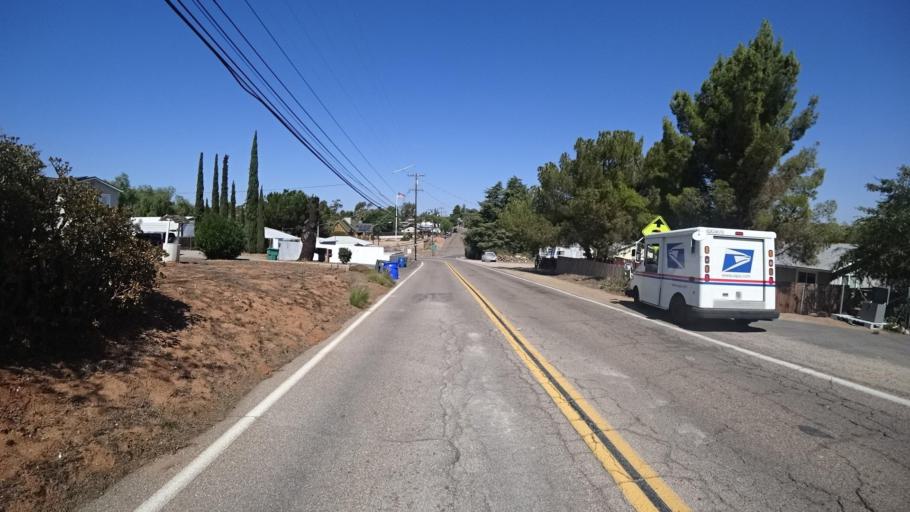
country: US
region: California
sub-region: San Diego County
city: Crest
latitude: 32.8139
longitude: -116.8621
